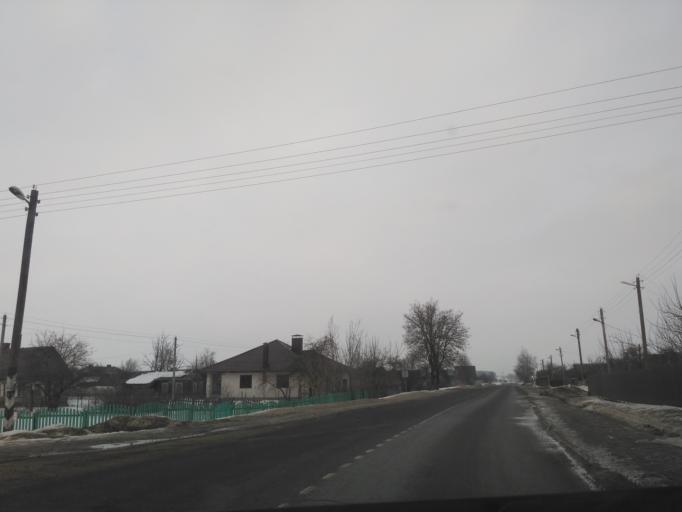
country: BY
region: Minsk
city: Horad Smalyavichy
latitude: 54.0260
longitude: 28.0644
